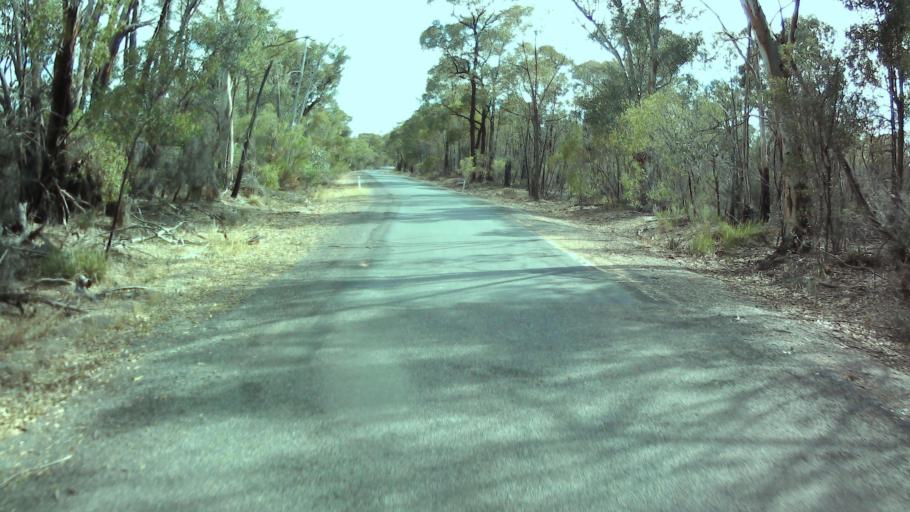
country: AU
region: New South Wales
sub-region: Weddin
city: Grenfell
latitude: -33.8693
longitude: 148.2046
